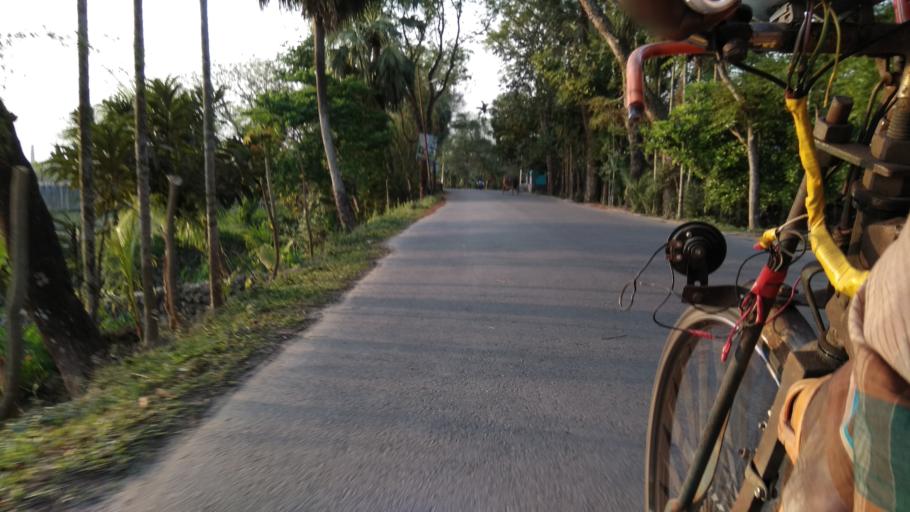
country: BD
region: Barisal
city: Mehendiganj
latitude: 22.9200
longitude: 90.4092
